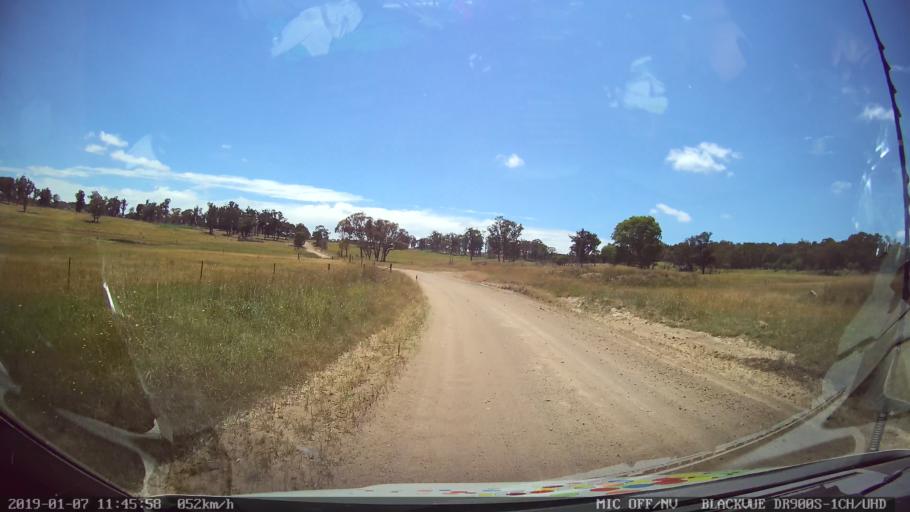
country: AU
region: New South Wales
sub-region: Guyra
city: Guyra
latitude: -30.3446
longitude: 151.6097
